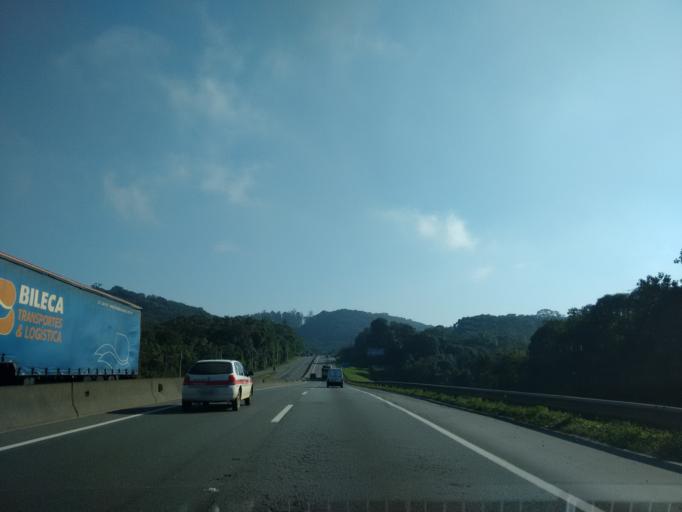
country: BR
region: Santa Catarina
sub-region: Joinville
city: Joinville
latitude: -26.2730
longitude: -48.8942
